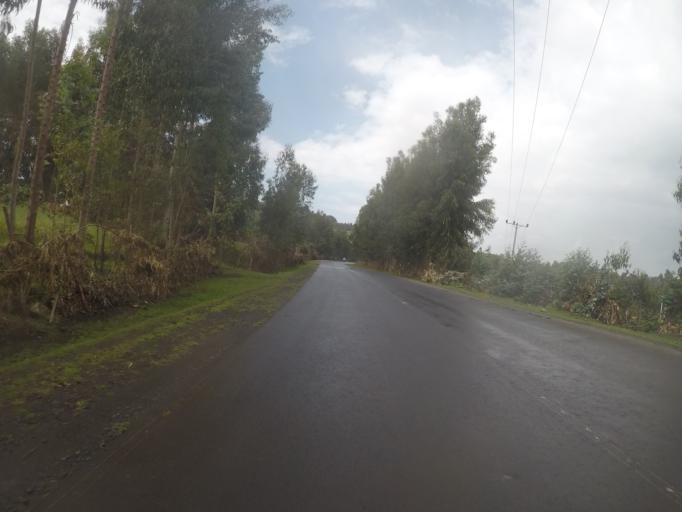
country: ET
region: Amhara
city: Debark'
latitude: 13.1152
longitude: 37.8706
